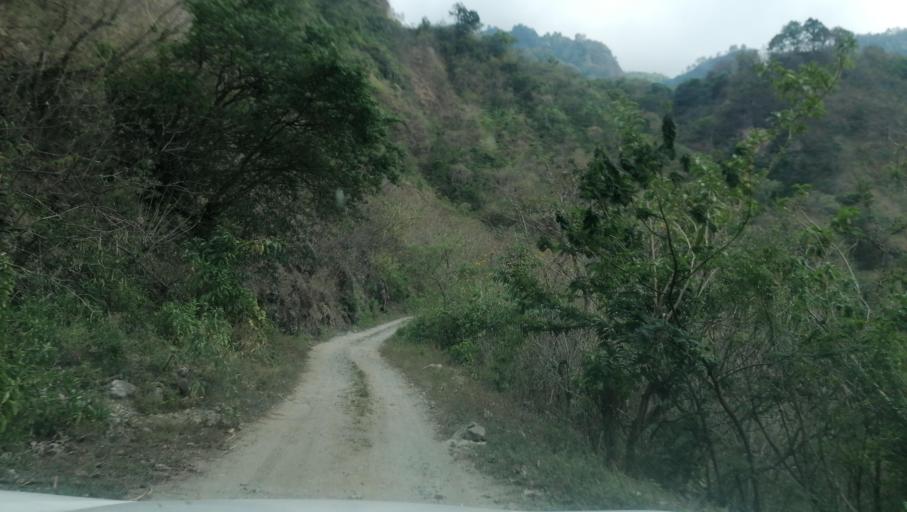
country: MX
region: Chiapas
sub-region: Cacahoatan
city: Benito Juarez
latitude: 15.1626
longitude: -92.1783
